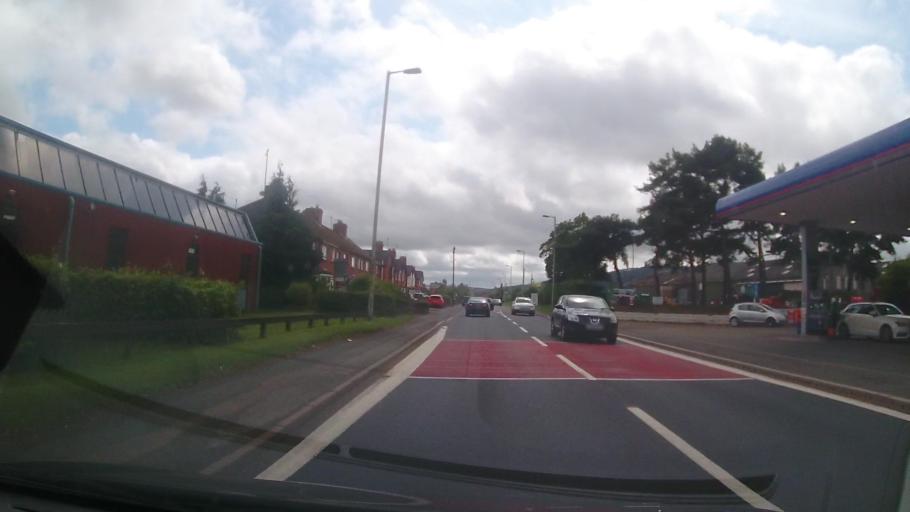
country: GB
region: England
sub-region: Shropshire
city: Craven Arms
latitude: 52.4460
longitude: -2.8371
